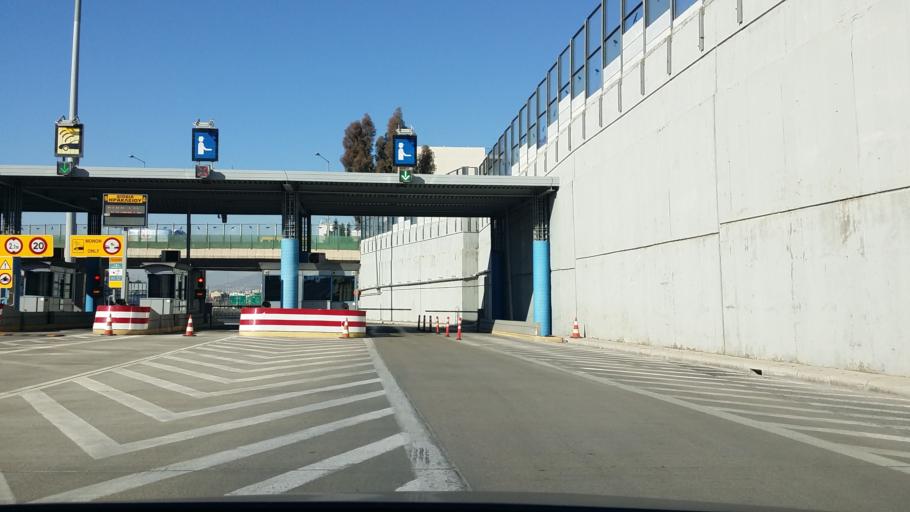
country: GR
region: Attica
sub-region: Nomarchia Athinas
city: Irakleio
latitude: 38.0584
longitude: 23.7694
